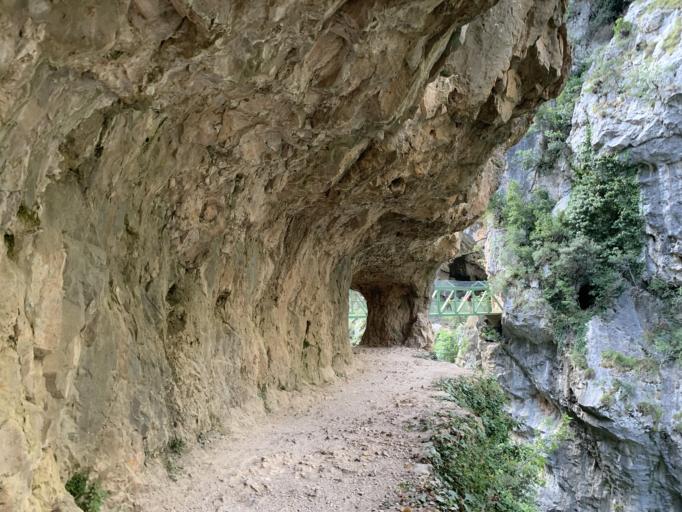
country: ES
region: Castille and Leon
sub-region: Provincia de Leon
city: Posada de Valdeon
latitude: 43.2252
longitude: -4.8970
